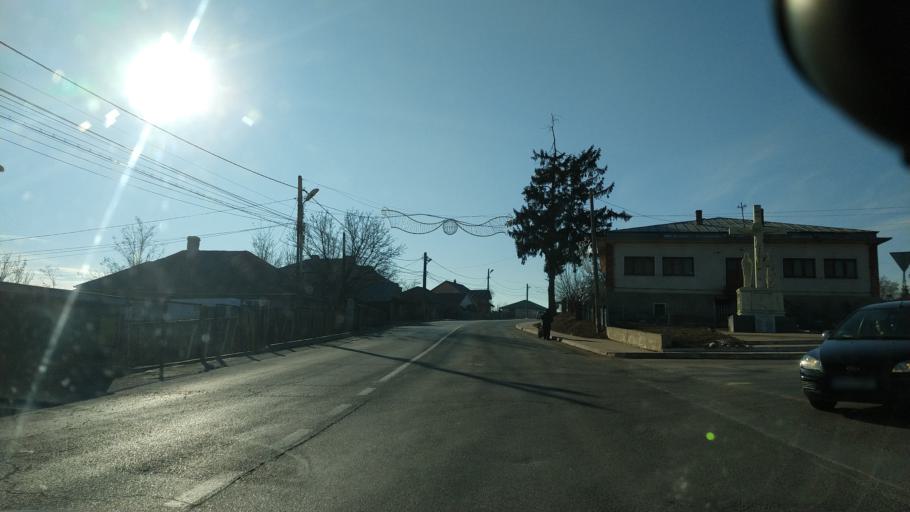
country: RO
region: Iasi
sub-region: Comuna Targu Frumos
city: Targu Frumos
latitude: 47.2042
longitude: 27.0074
